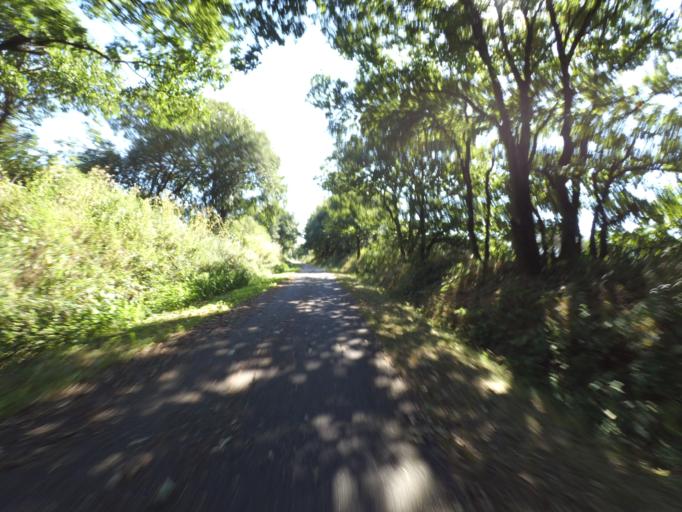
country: DE
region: Rheinland-Pfalz
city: Niederofflingen
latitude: 50.0648
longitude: 6.8990
